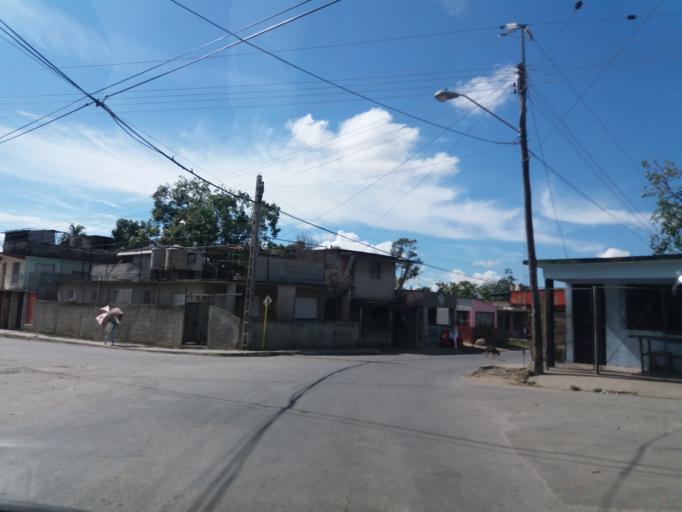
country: CU
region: Cienfuegos
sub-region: Municipio de Cienfuegos
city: Cienfuegos
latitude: 22.1471
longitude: -80.4256
